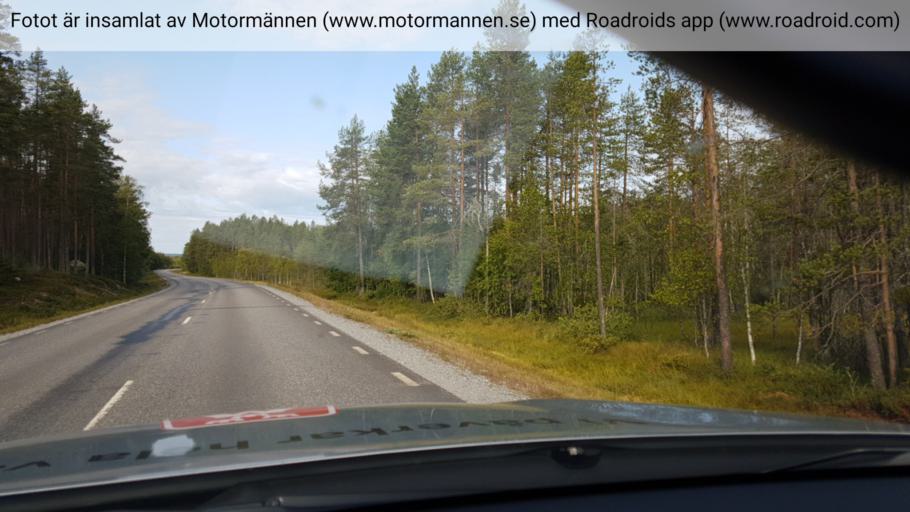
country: SE
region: Norrbotten
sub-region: Pitea Kommun
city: Roknas
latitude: 65.3424
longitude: 20.9817
